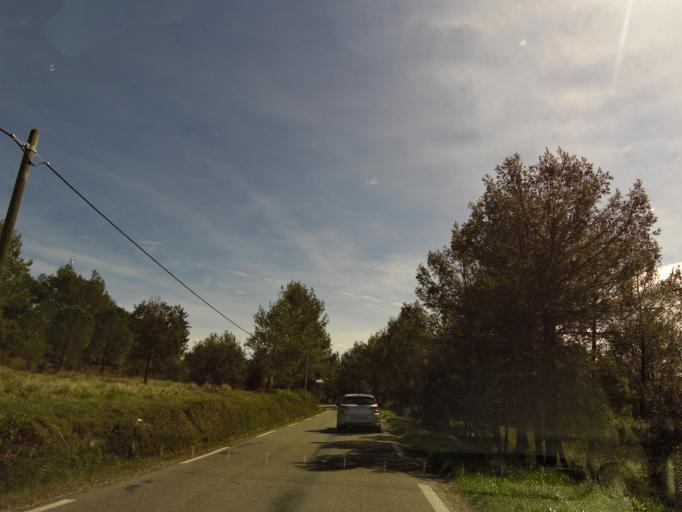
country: FR
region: Languedoc-Roussillon
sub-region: Departement du Gard
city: Bernis
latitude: 43.7797
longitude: 4.2752
